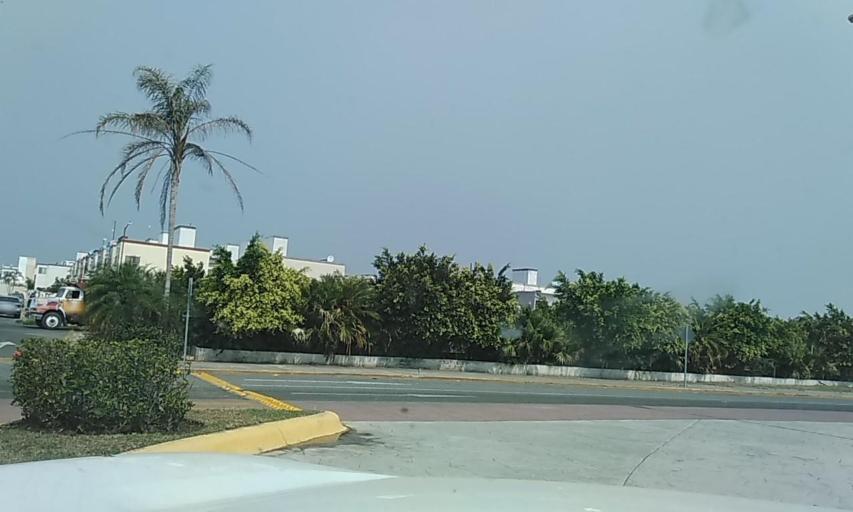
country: MX
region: Veracruz
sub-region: Veracruz
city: Hacienda Sotavento
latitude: 19.1332
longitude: -96.1738
